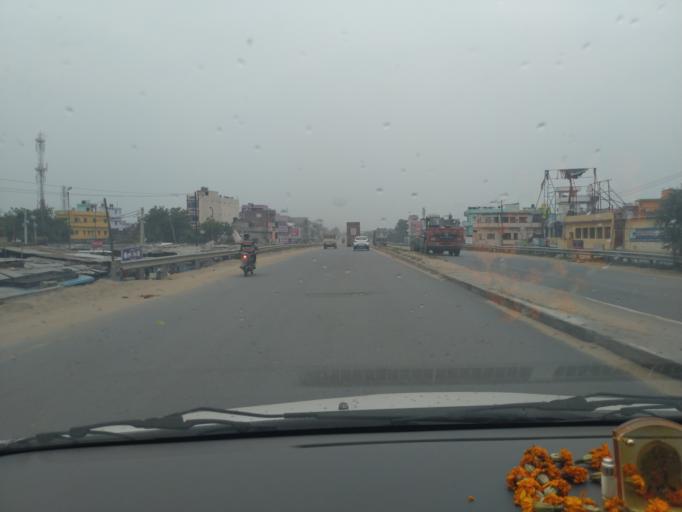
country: IN
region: Bihar
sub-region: Rohtas
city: Dehri
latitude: 24.9079
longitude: 84.1844
